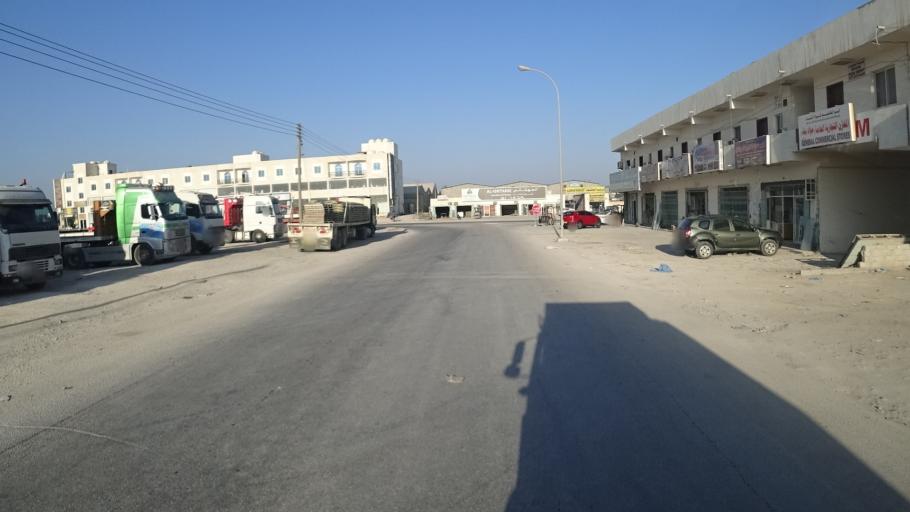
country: OM
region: Zufar
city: Salalah
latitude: 17.0250
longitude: 54.0457
